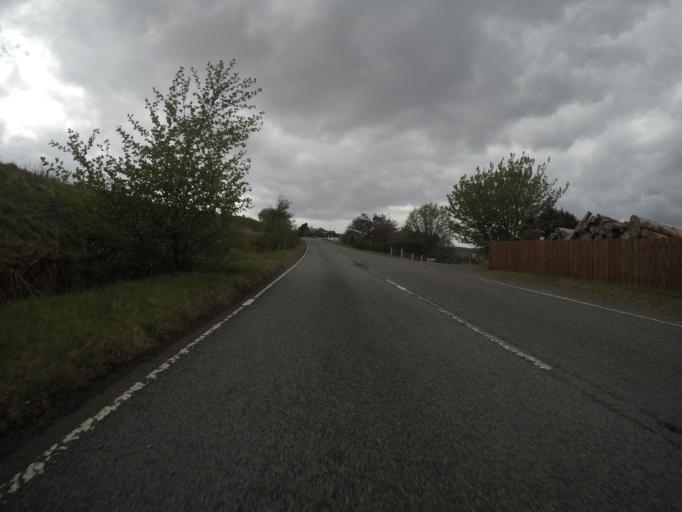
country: GB
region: Scotland
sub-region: Highland
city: Isle of Skye
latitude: 57.2959
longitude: -6.3286
